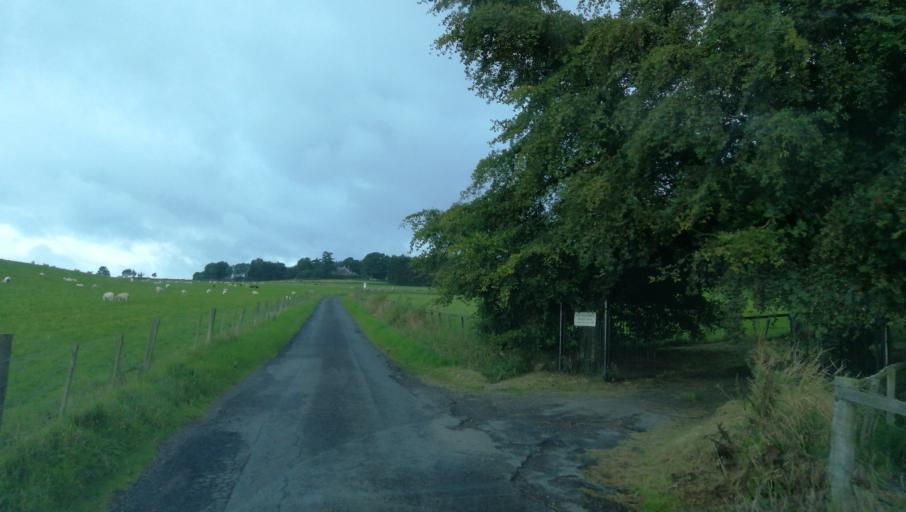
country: GB
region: Scotland
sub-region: Perth and Kinross
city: Alyth
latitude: 56.6260
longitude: -3.2726
